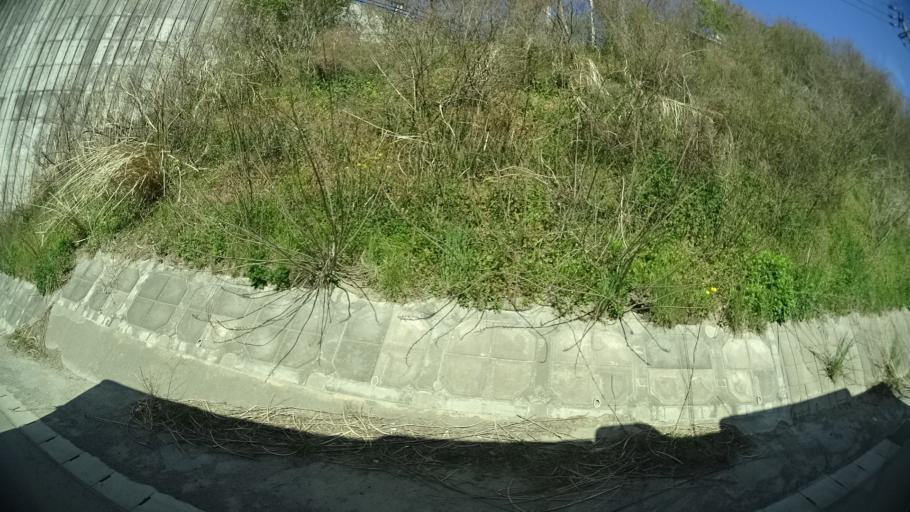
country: JP
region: Iwate
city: Ofunato
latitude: 39.0267
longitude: 141.6258
